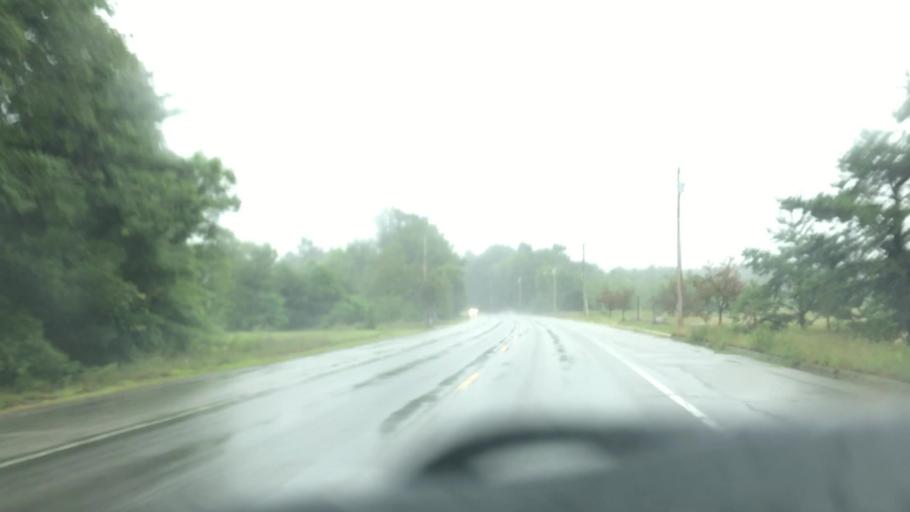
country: US
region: Maine
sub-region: York County
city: North Berwick
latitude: 43.3071
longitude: -70.6628
